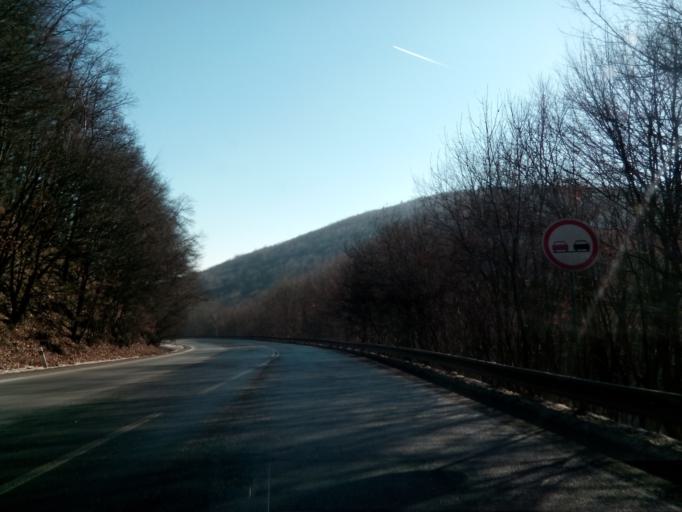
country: SK
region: Kosicky
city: Secovce
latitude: 48.7349
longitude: 21.5484
